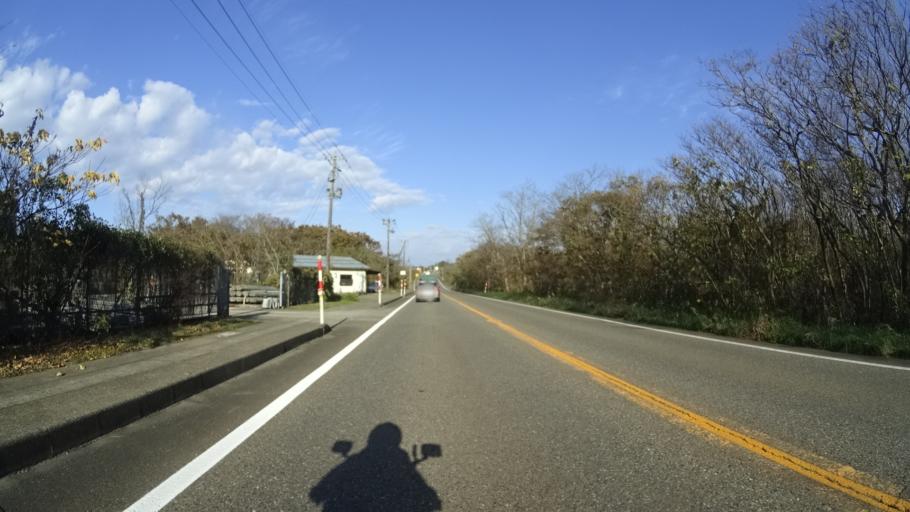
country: JP
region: Niigata
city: Joetsu
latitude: 37.2607
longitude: 138.3706
